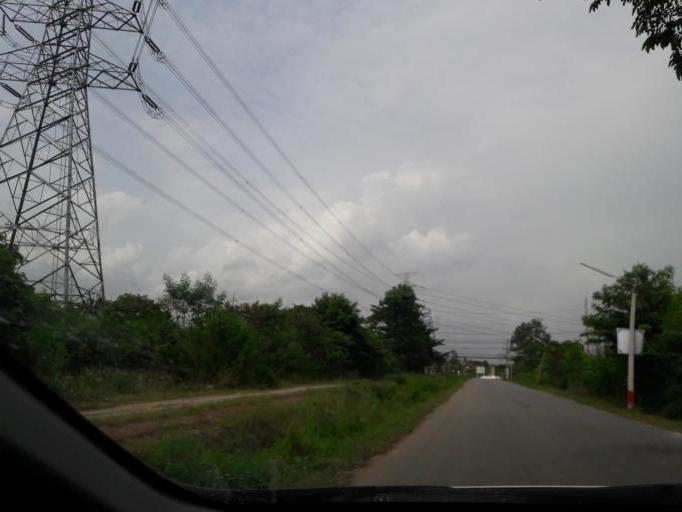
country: TH
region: Ratchaburi
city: Ratchaburi
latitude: 13.5132
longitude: 99.7888
